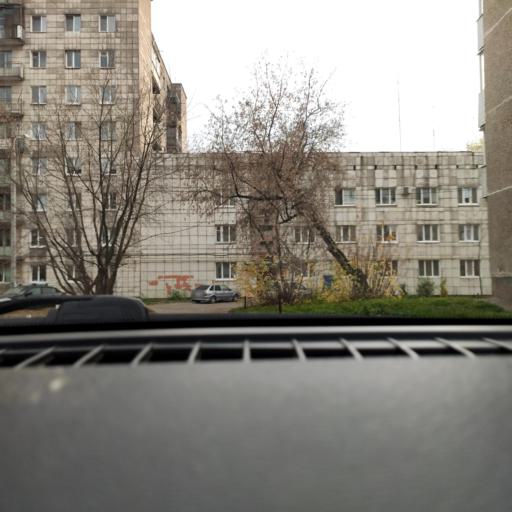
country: RU
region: Perm
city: Perm
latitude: 57.9613
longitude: 56.2173
